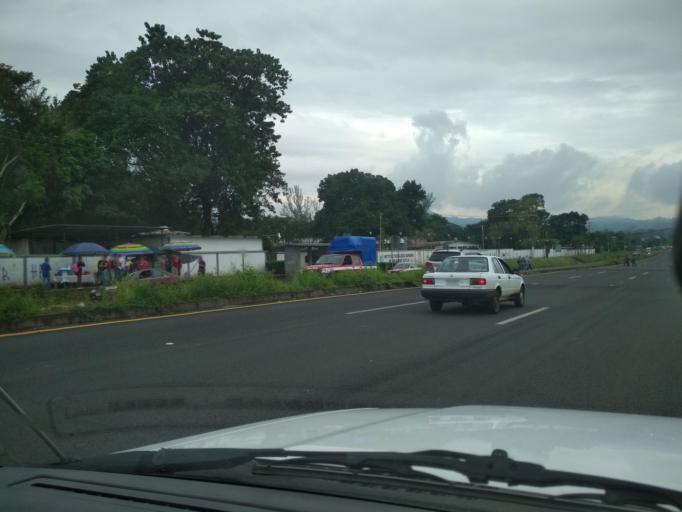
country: MX
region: Veracruz
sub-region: San Andres Tuxtla
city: Matacapan
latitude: 18.4352
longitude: -95.1706
